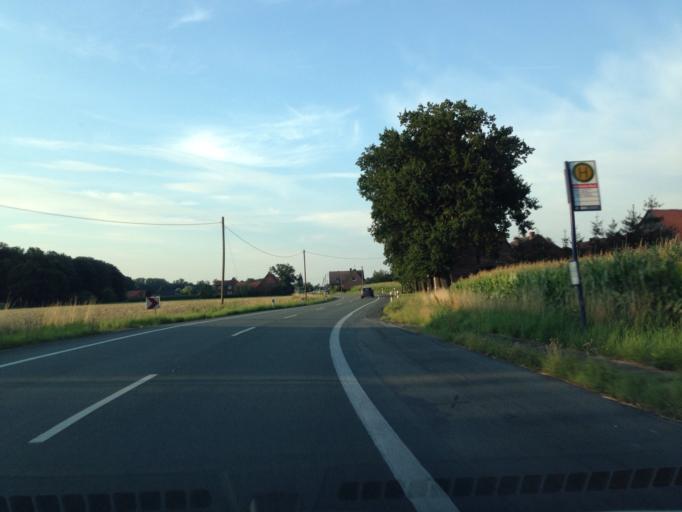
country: DE
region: North Rhine-Westphalia
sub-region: Regierungsbezirk Munster
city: Senden
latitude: 51.8456
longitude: 7.5431
